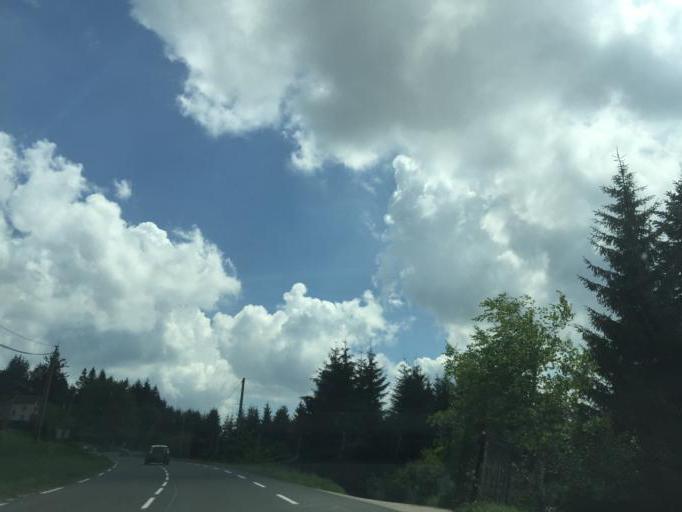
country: FR
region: Rhone-Alpes
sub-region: Departement de la Loire
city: Saint-Genest-Malifaux
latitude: 45.3745
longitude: 4.4452
